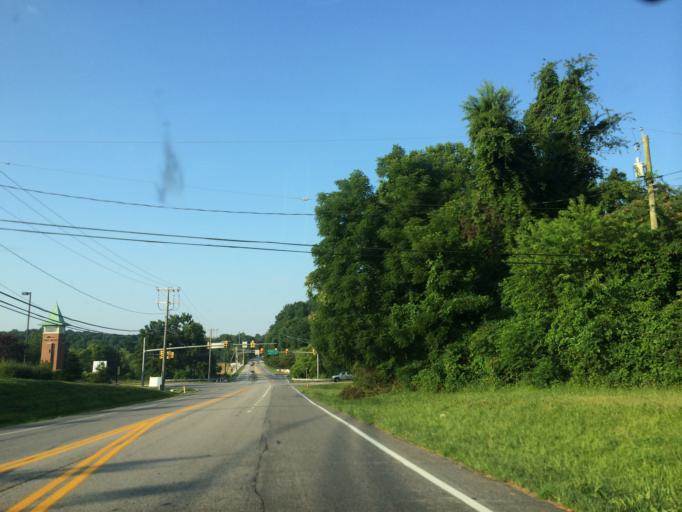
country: US
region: Maryland
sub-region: Howard County
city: Columbia
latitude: 39.3014
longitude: -76.9001
